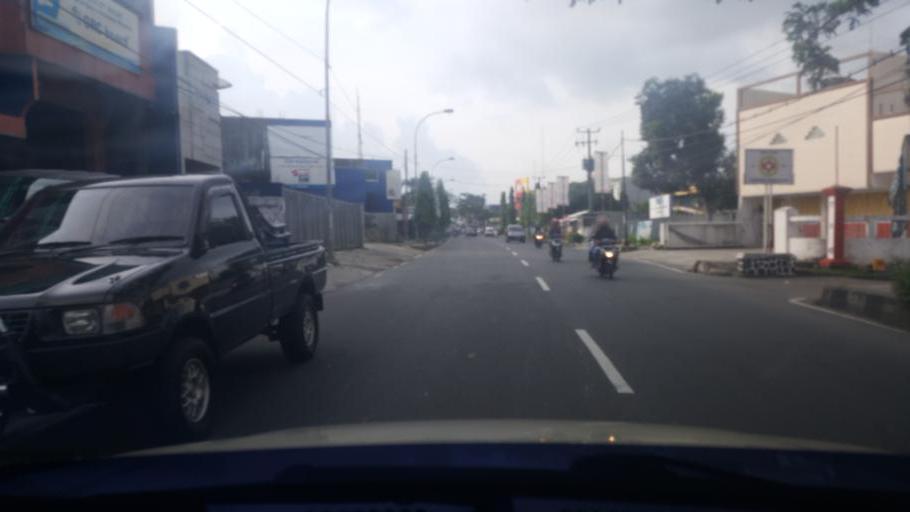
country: ID
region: West Java
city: Leuwidahu
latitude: -7.3078
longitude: 108.2085
